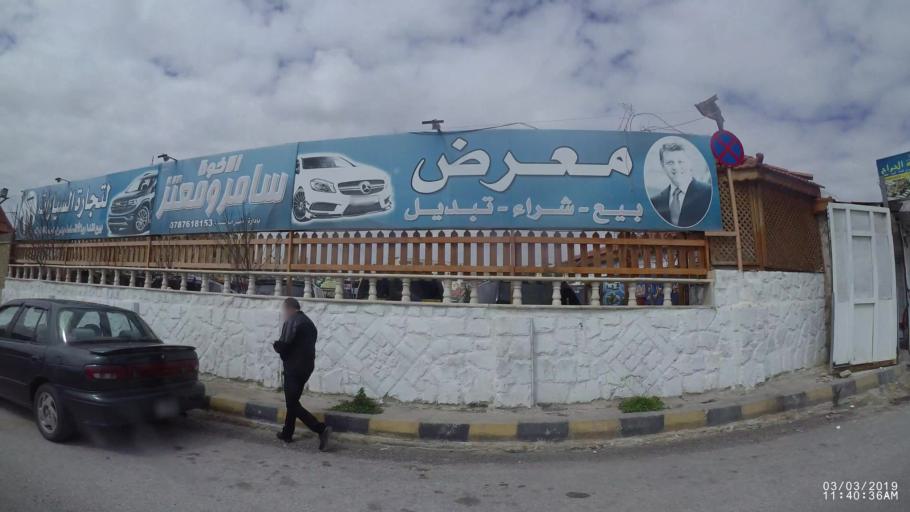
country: JO
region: Amman
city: Amman
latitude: 31.9942
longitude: 35.9181
